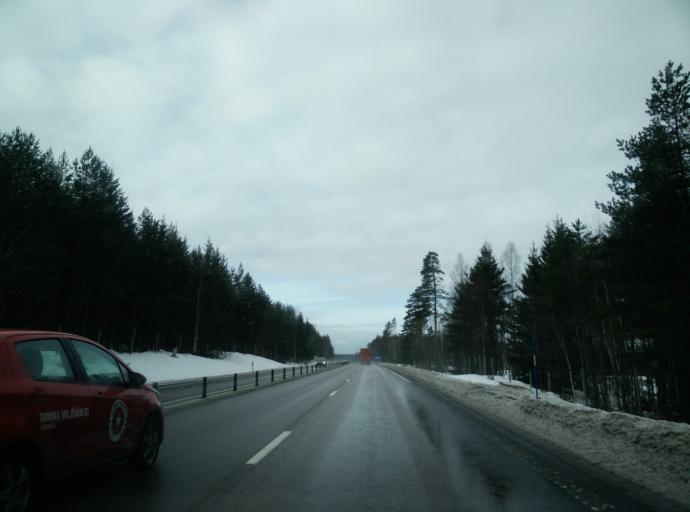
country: SE
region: Dalarna
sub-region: Hedemora Kommun
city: Langshyttan
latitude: 60.5564
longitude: 16.0618
